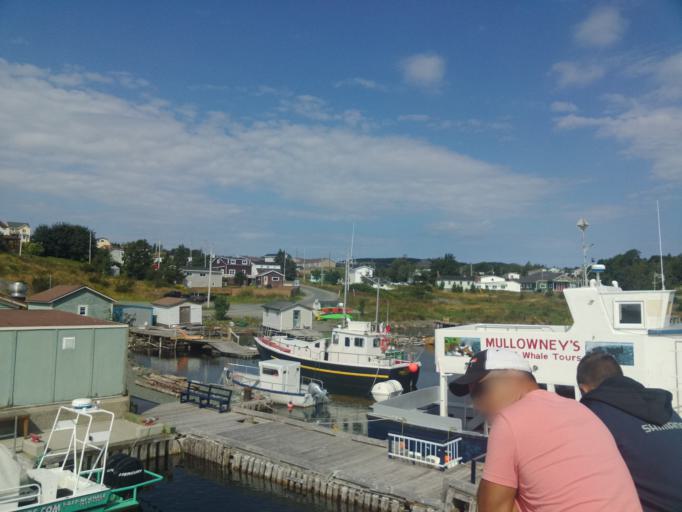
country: CA
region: Newfoundland and Labrador
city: Mount Pearl
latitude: 47.3152
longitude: -52.8133
